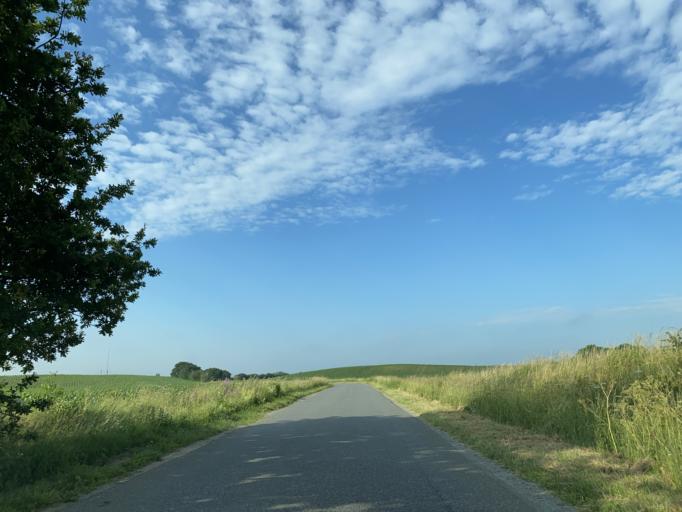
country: DK
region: South Denmark
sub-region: Haderslev Kommune
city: Haderslev
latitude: 55.1939
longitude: 9.4714
